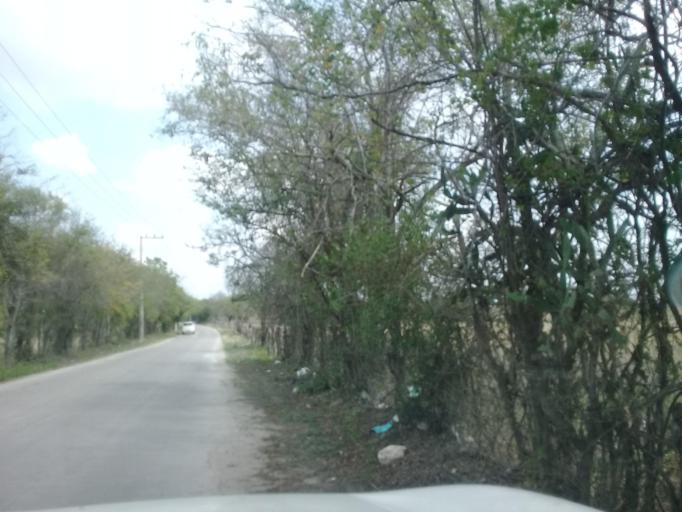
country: MX
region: Veracruz
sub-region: Emiliano Zapata
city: Plan del Rio
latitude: 19.3579
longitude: -96.6541
